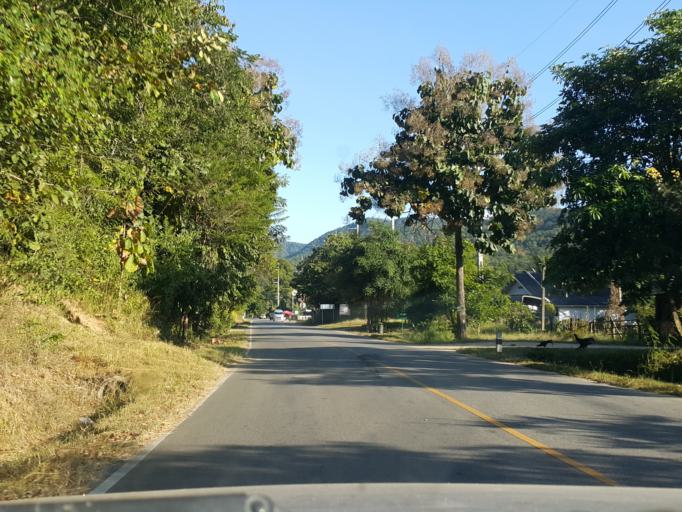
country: TH
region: Mae Hong Son
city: Mae Hi
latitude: 19.2864
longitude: 98.4745
